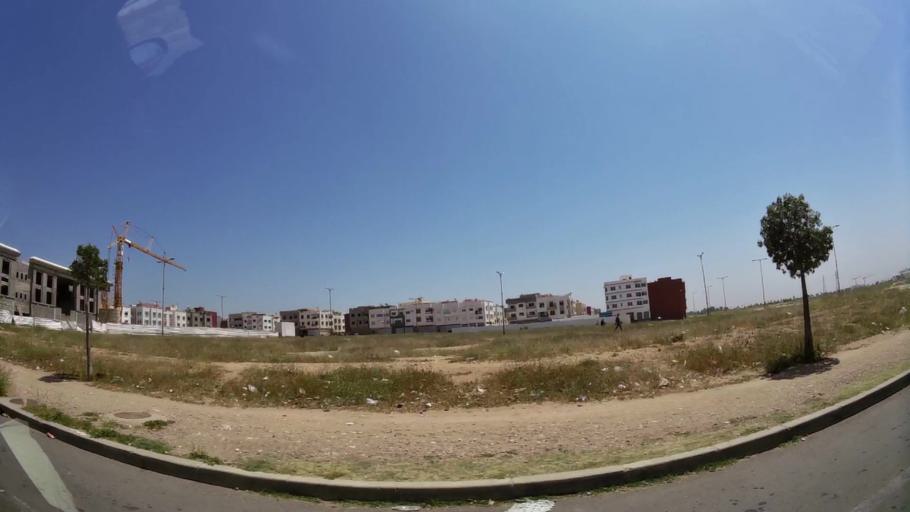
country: MA
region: Oued ed Dahab-Lagouira
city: Dakhla
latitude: 30.4269
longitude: -9.5565
